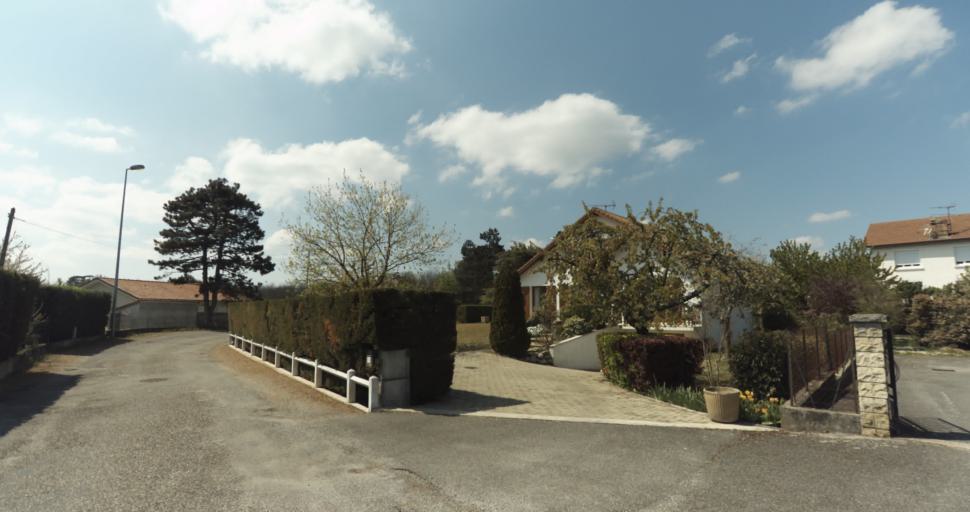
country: FR
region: Rhone-Alpes
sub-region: Departement de l'Isere
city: Saint-Marcellin
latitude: 45.1455
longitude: 5.3221
